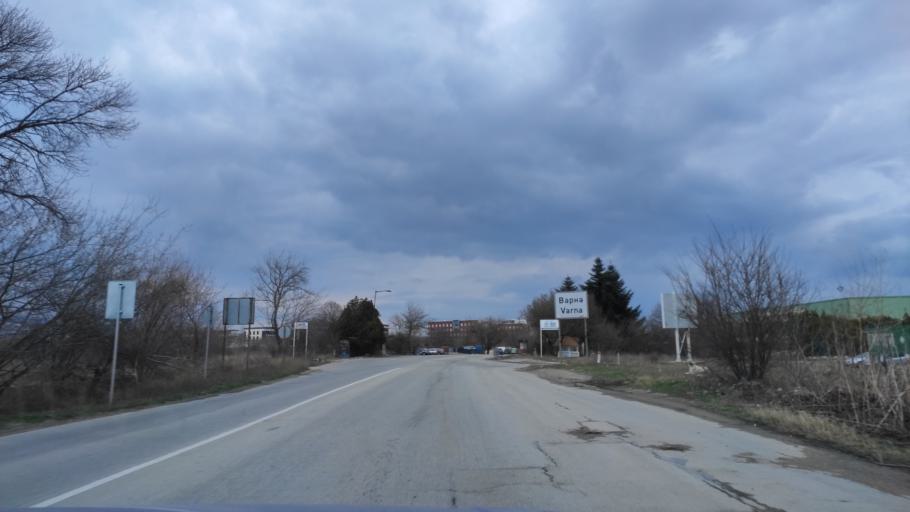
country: BG
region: Varna
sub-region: Obshtina Aksakovo
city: Aksakovo
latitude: 43.2276
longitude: 27.8513
